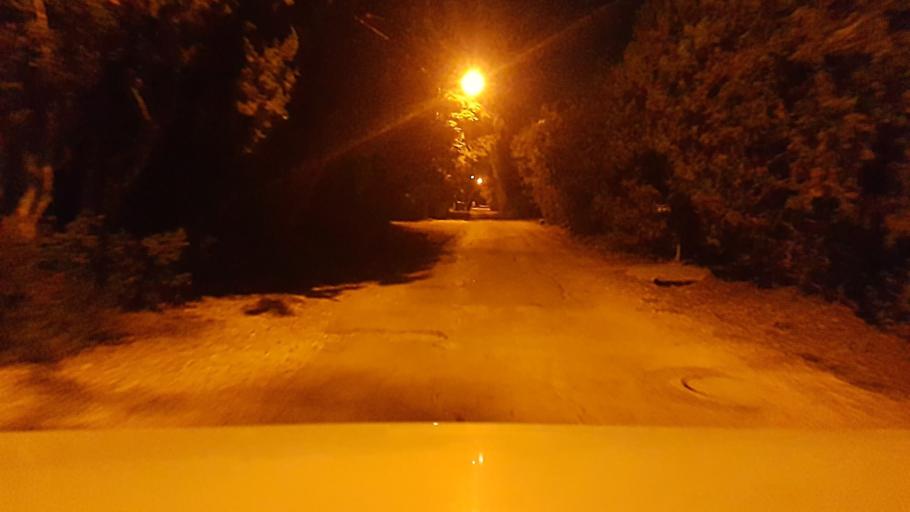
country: IL
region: Central District
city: Nehalim
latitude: 32.0801
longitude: 34.9209
